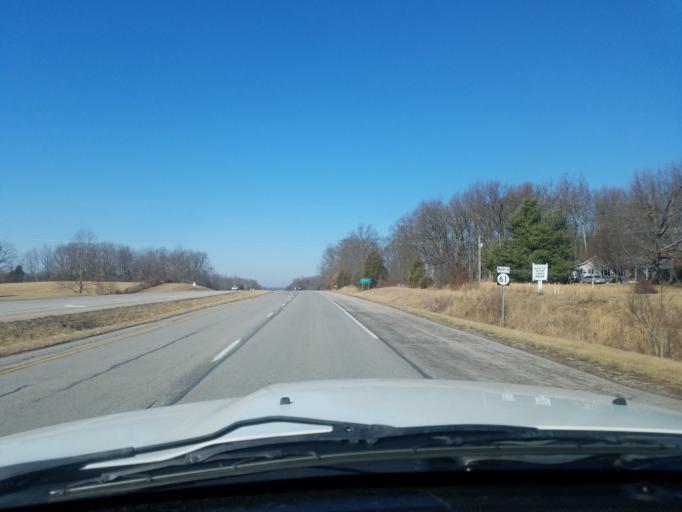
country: US
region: Kentucky
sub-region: Hardin County
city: Elizabethtown
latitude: 37.6297
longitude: -85.8216
